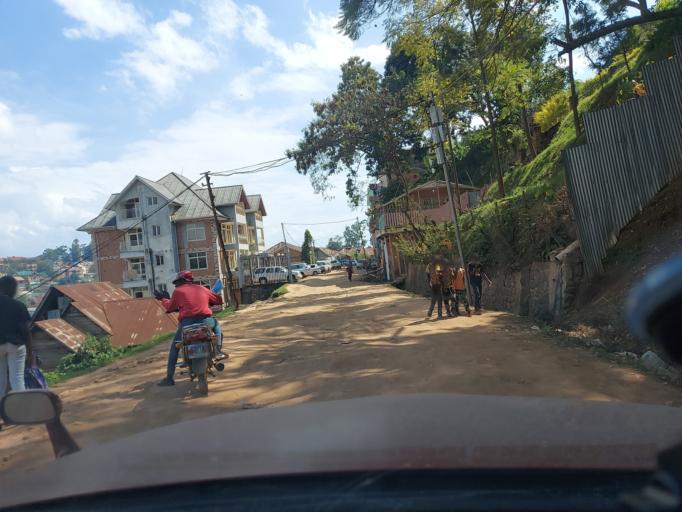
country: CD
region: South Kivu
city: Bukavu
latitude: -2.5014
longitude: 28.8646
